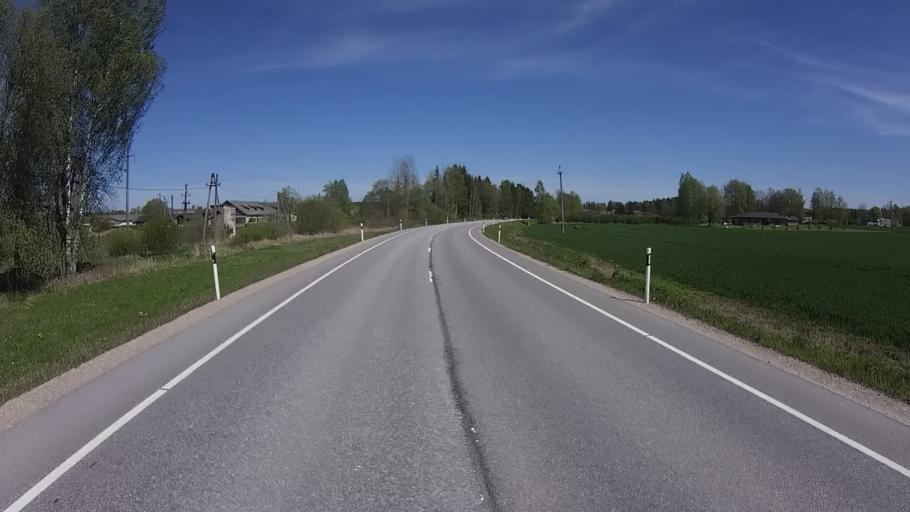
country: EE
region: Vorumaa
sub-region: Voru linn
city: Voru
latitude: 57.8700
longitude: 27.1085
